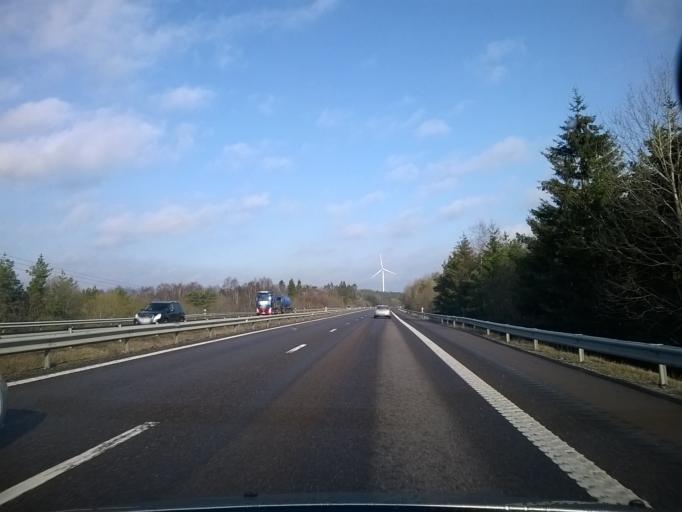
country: SE
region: Vaestra Goetaland
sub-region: Kungalvs Kommun
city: Kode
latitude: 57.9124
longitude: 11.8926
